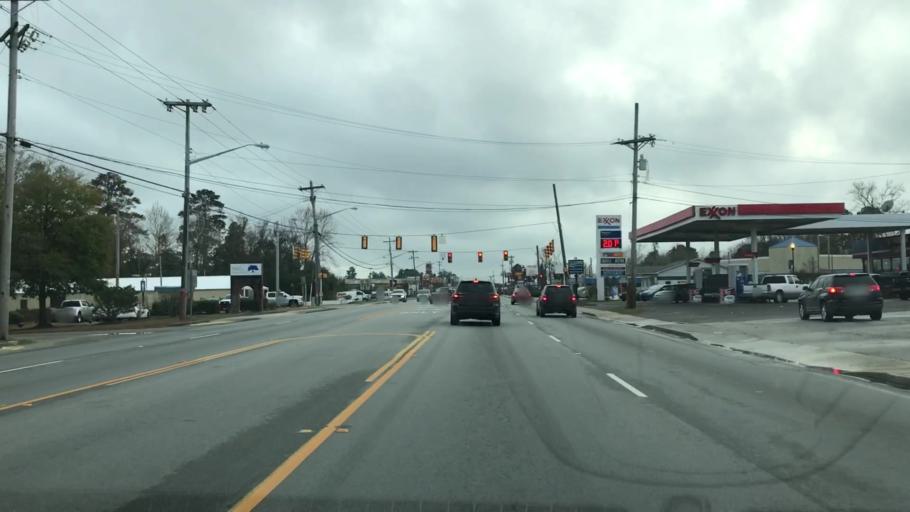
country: US
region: South Carolina
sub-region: Berkeley County
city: Moncks Corner
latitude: 33.1928
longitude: -79.9961
